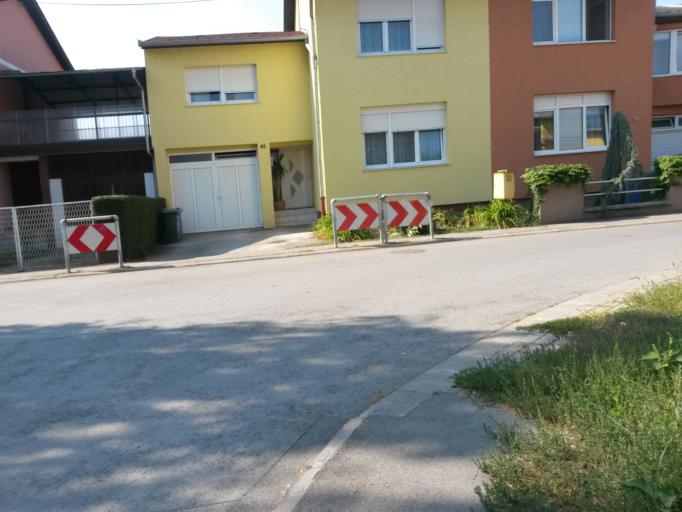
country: HR
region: Osjecko-Baranjska
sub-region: Grad Osijek
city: Osijek
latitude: 45.5445
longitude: 18.6722
